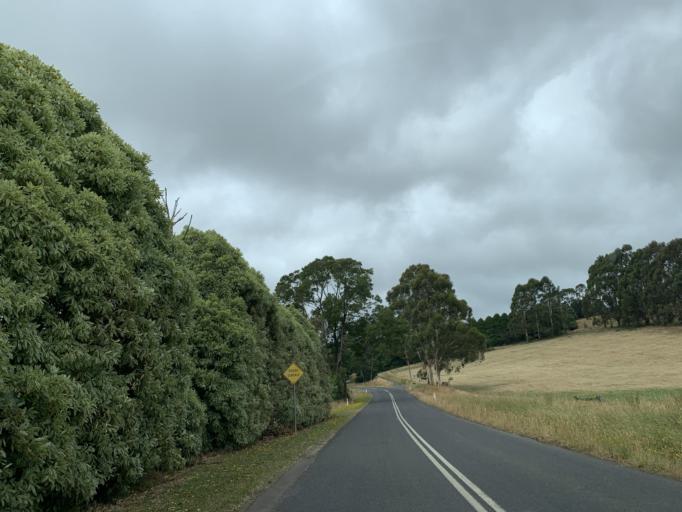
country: AU
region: Victoria
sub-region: Baw Baw
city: Warragul
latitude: -38.2442
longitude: 146.0047
